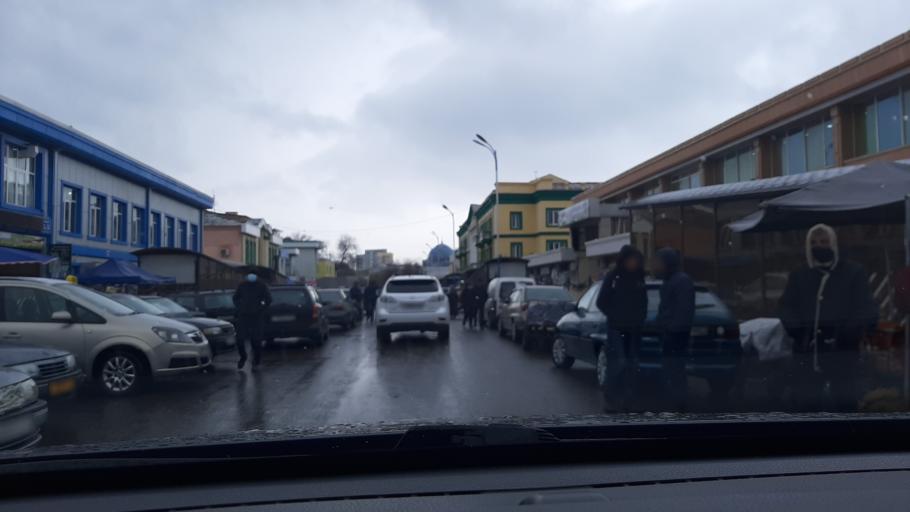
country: TJ
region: Viloyati Sughd
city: Khujand
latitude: 40.2784
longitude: 69.6342
